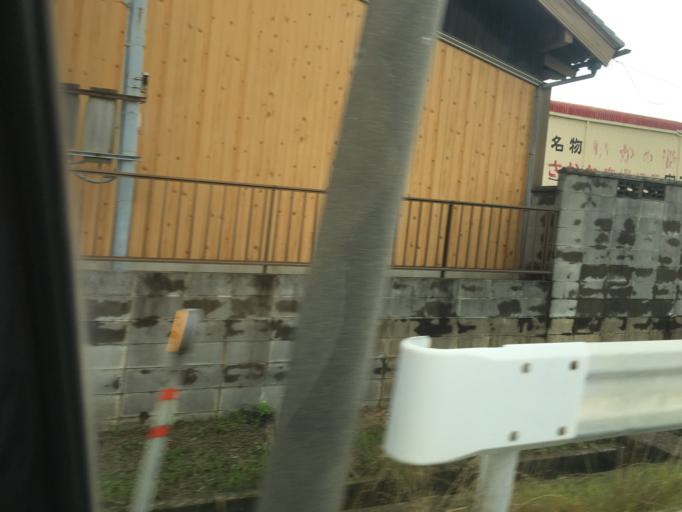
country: JP
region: Aichi
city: Ishiki
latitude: 34.8069
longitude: 137.0196
